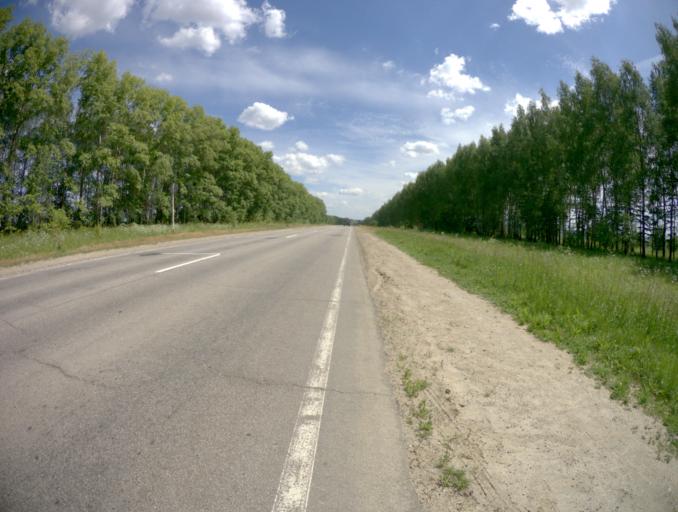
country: RU
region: Ivanovo
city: Gavrilov Posad
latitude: 56.3789
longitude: 40.0124
